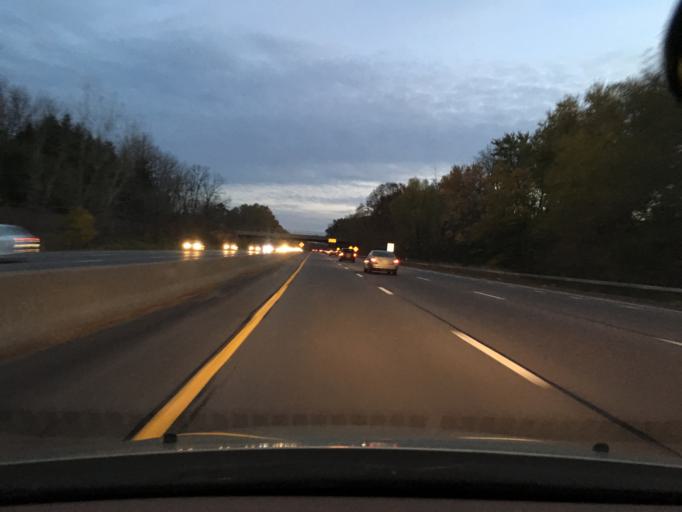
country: US
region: New York
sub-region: Monroe County
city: Pittsford
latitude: 43.1055
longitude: -77.5062
